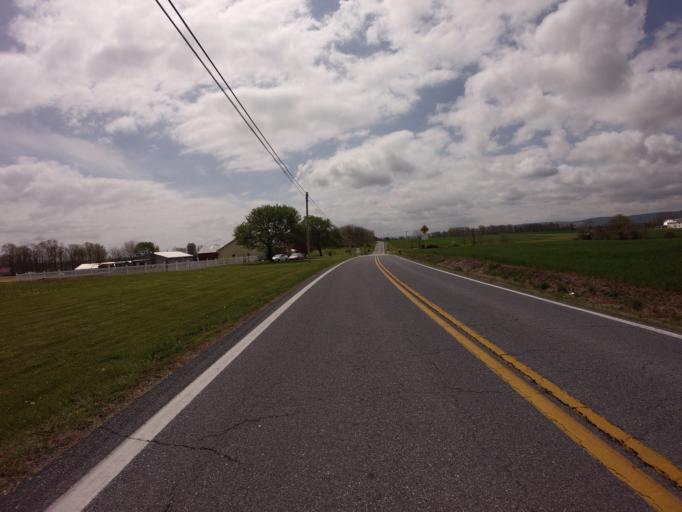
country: US
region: Maryland
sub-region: Frederick County
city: Emmitsburg
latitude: 39.6621
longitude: -77.3373
